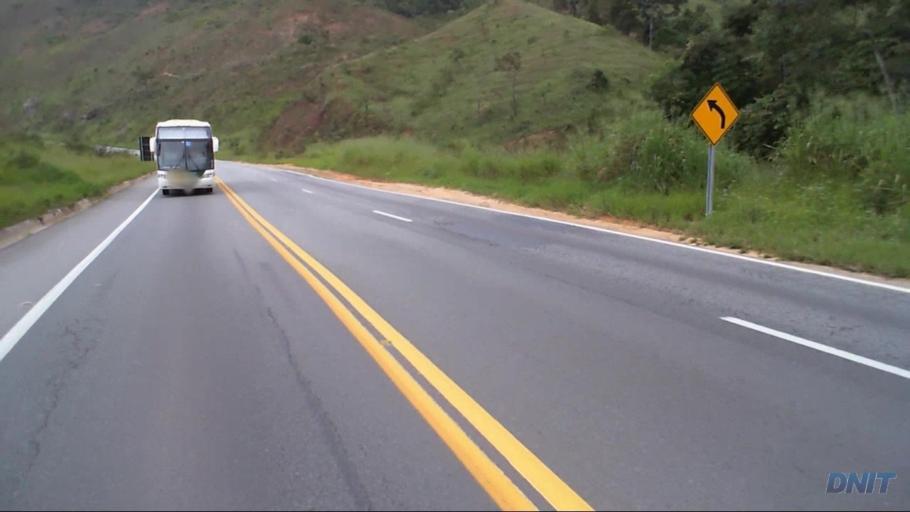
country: BR
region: Minas Gerais
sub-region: Nova Era
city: Nova Era
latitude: -19.6423
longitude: -42.9124
